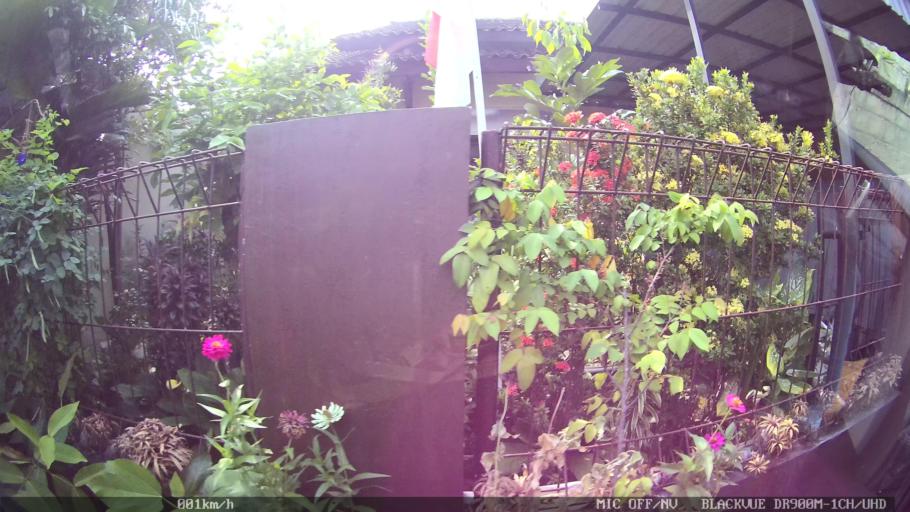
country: ID
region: Daerah Istimewa Yogyakarta
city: Yogyakarta
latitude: -7.8119
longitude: 110.3797
